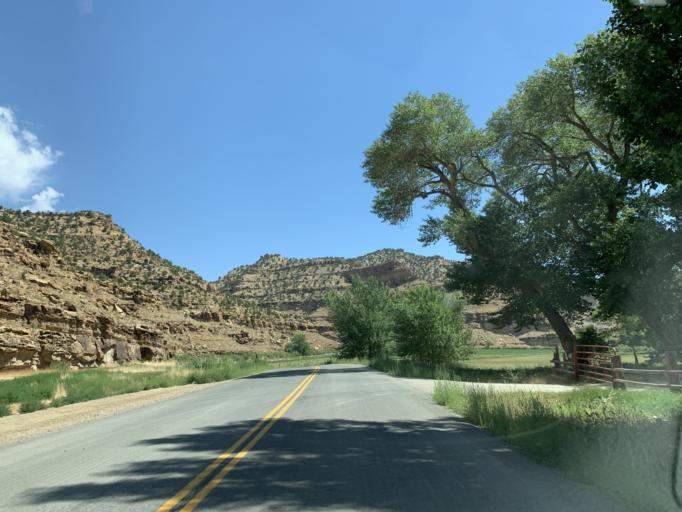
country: US
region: Utah
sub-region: Carbon County
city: East Carbon City
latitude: 39.8088
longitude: -110.2570
